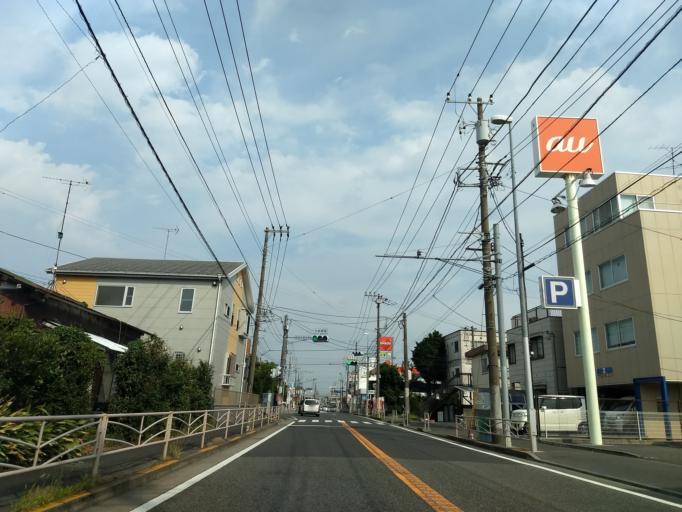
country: JP
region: Kanagawa
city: Minami-rinkan
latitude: 35.4802
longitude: 139.5356
